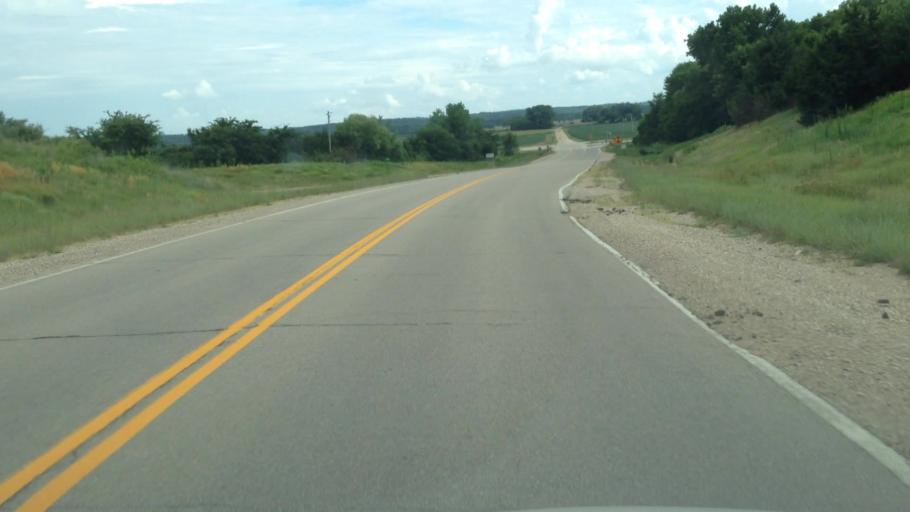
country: US
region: Kansas
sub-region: Jefferson County
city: Oskaloosa
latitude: 39.0897
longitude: -95.4740
